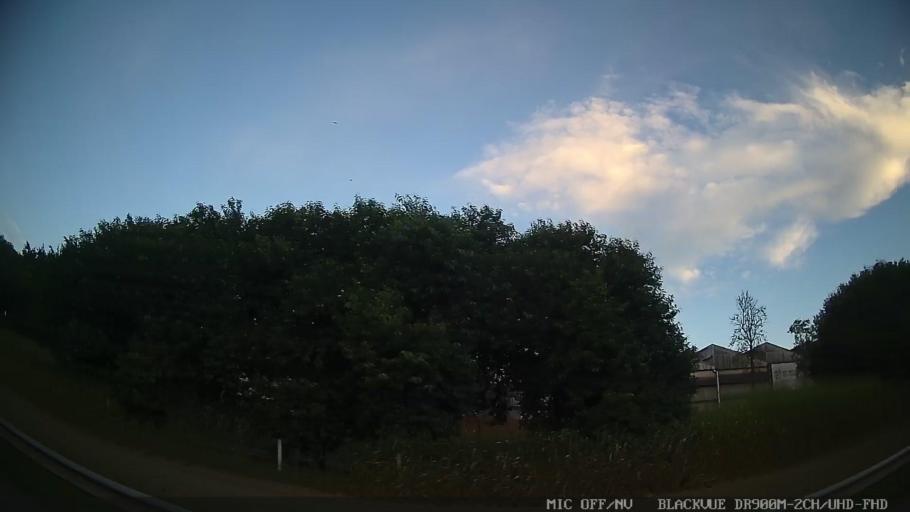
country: BR
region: Sao Paulo
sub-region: Indaiatuba
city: Indaiatuba
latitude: -23.1330
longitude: -47.2366
